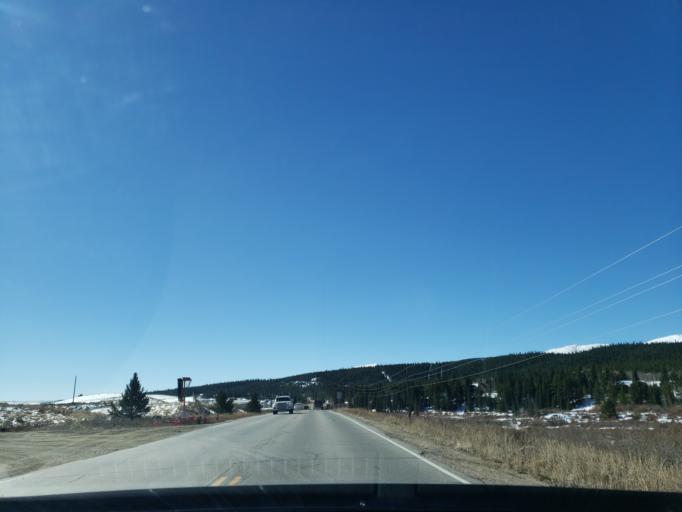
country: US
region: Colorado
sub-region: Park County
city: Fairplay
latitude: 39.2989
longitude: -106.0644
